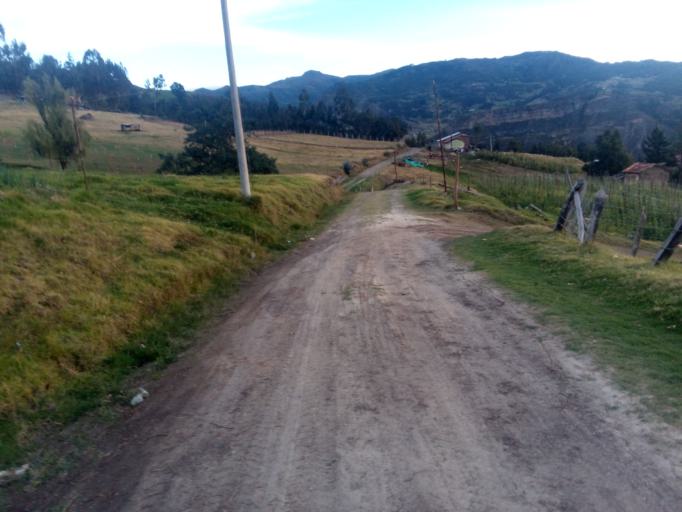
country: CO
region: Boyaca
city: Gameza
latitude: 5.8007
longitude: -72.8026
